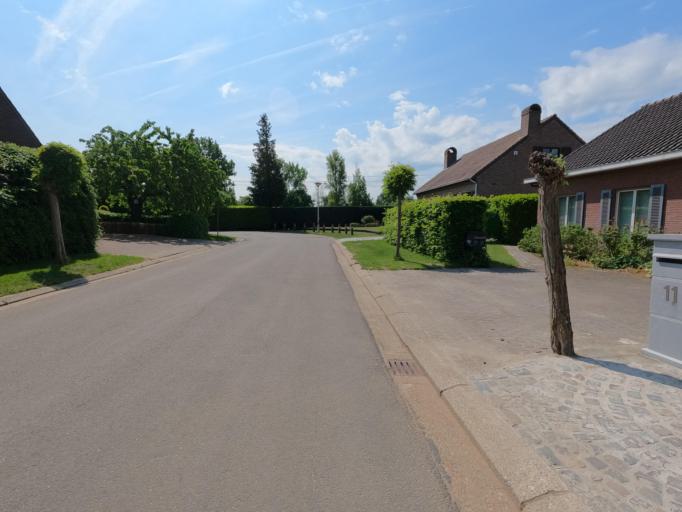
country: BE
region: Flanders
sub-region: Provincie Antwerpen
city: Grobbendonk
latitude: 51.1656
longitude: 4.7403
